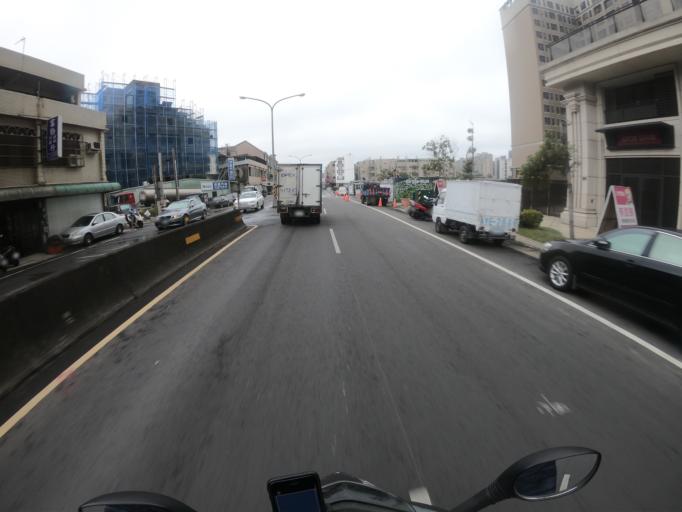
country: TW
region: Taiwan
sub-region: Hsinchu
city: Zhubei
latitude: 24.8265
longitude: 121.0041
